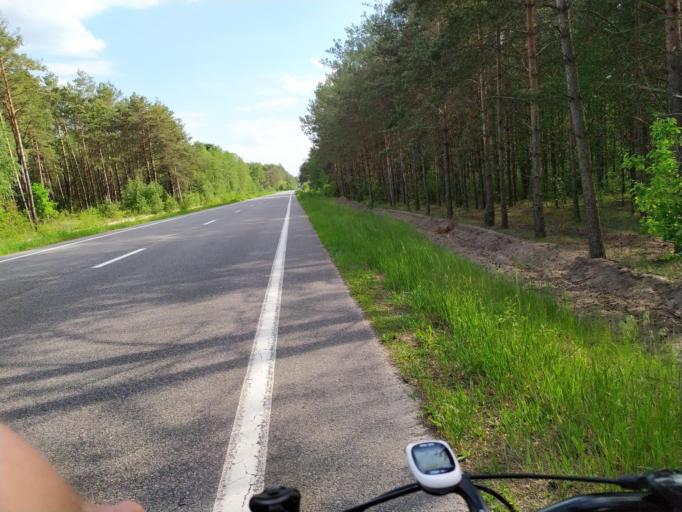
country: BY
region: Brest
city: Zhabinka
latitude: 52.4294
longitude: 24.1251
